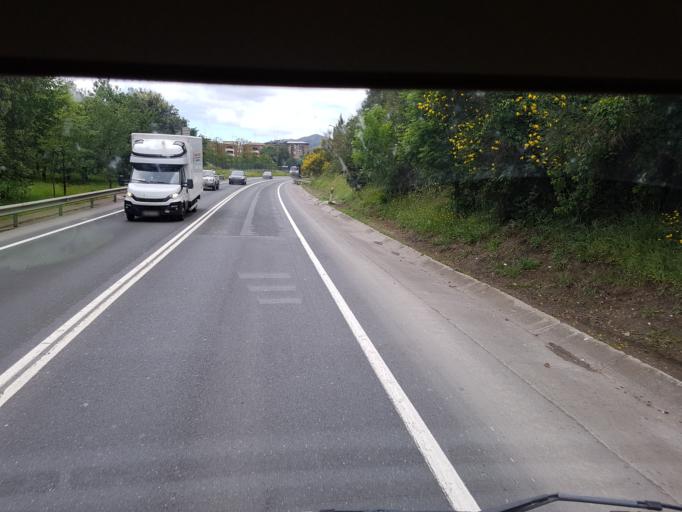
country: ES
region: Basque Country
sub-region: Bizkaia
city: Amorebieta
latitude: 43.2146
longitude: -2.7230
